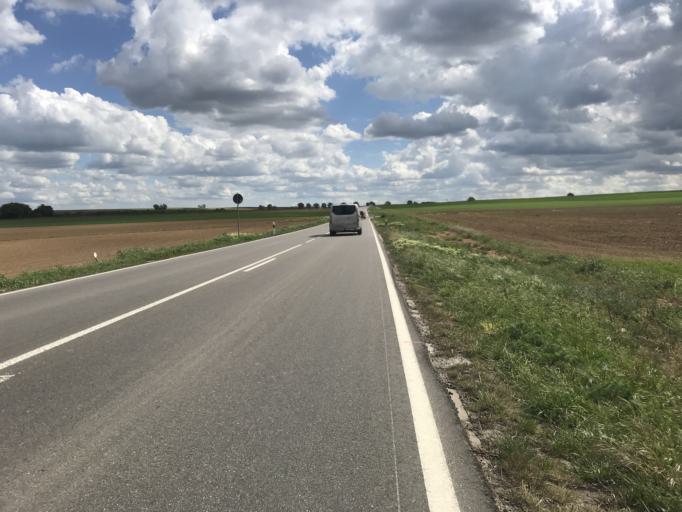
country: DE
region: Rheinland-Pfalz
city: Gau-Bischofsheim
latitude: 49.9384
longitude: 8.2642
